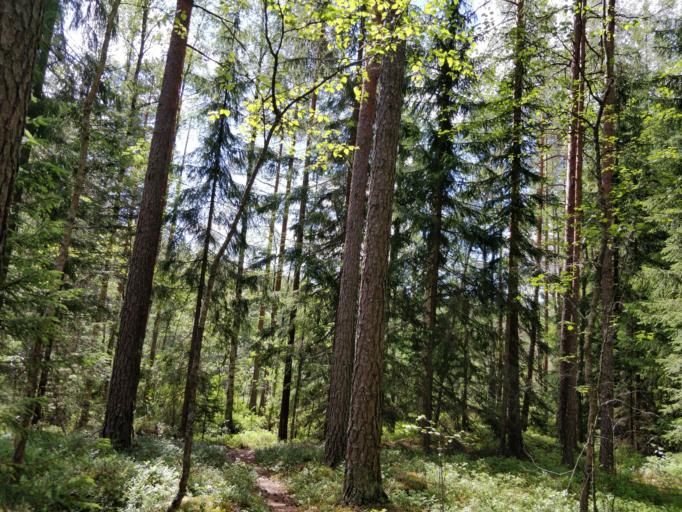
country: FI
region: Uusimaa
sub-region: Helsinki
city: Vihti
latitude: 60.3133
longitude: 24.4699
